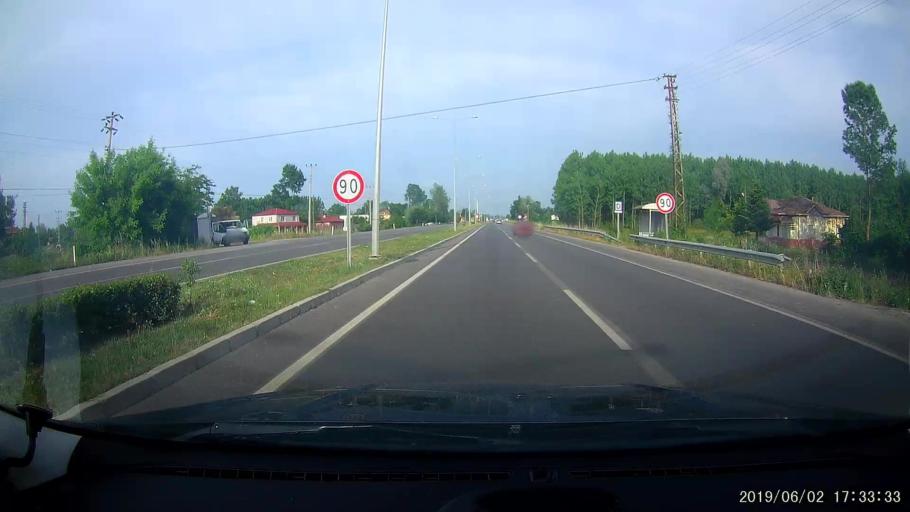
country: TR
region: Samsun
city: Terme
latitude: 41.2208
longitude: 36.8511
